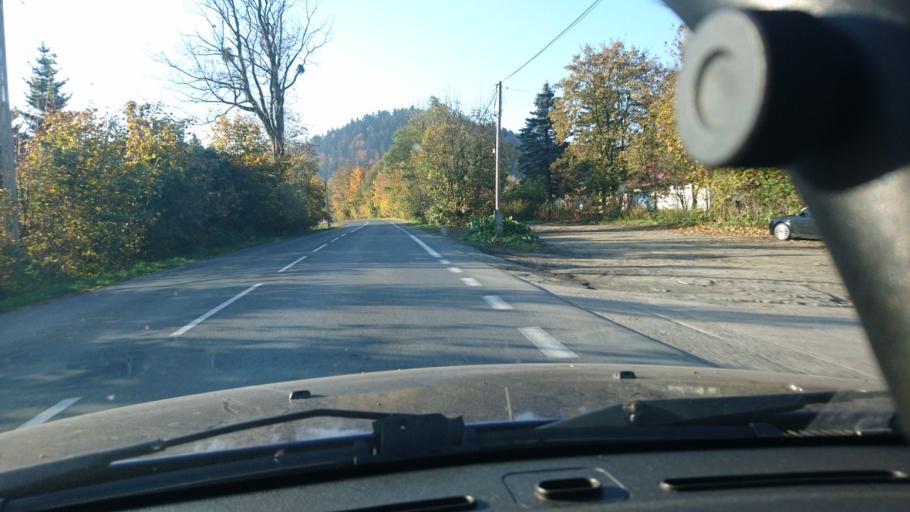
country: PL
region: Silesian Voivodeship
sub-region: Powiat cieszynski
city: Wisla
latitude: 49.6705
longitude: 18.8465
